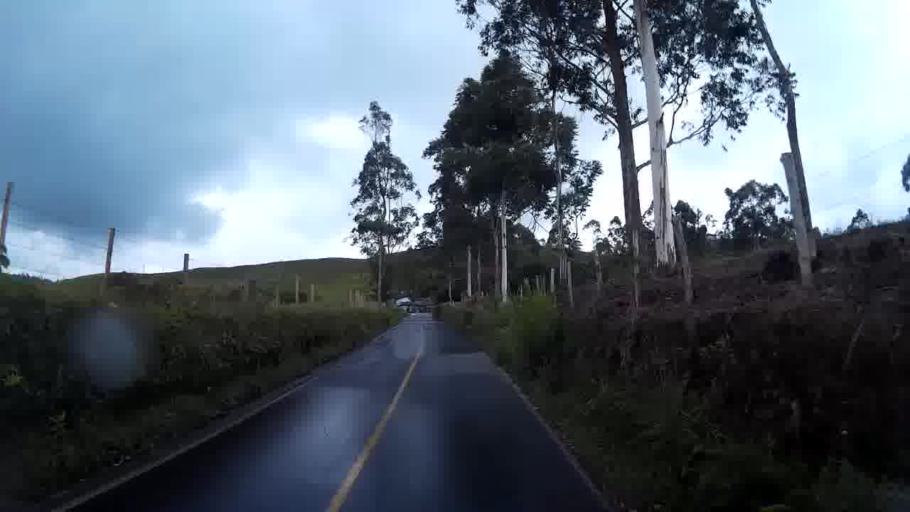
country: CO
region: Quindio
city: Filandia
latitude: 4.6845
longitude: -75.6584
